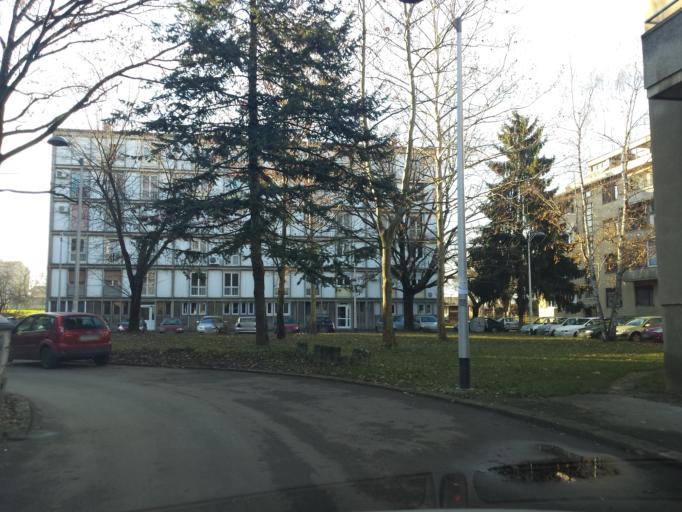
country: HR
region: Grad Zagreb
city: Jankomir
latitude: 45.8023
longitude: 15.9267
